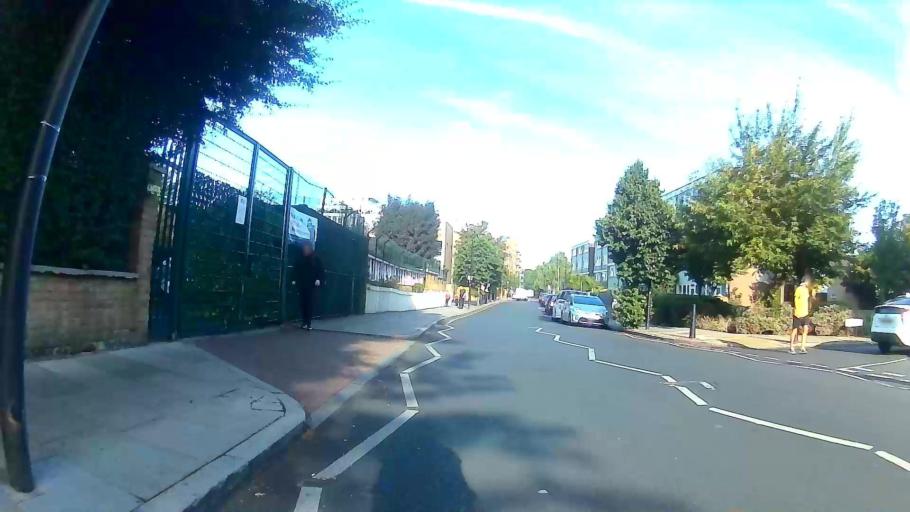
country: GB
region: England
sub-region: Greater London
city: Poplar
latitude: 51.5137
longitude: -0.0180
